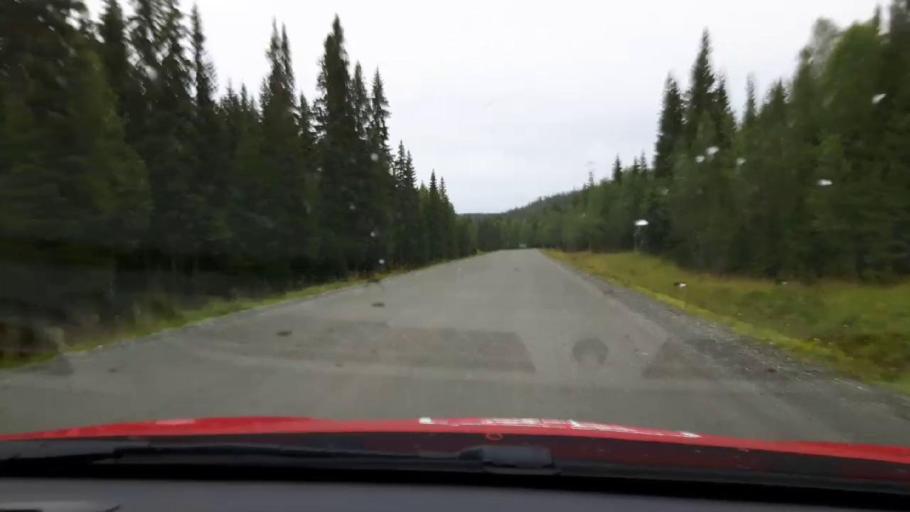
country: SE
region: Jaemtland
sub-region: Are Kommun
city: Are
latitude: 63.4185
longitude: 12.7564
